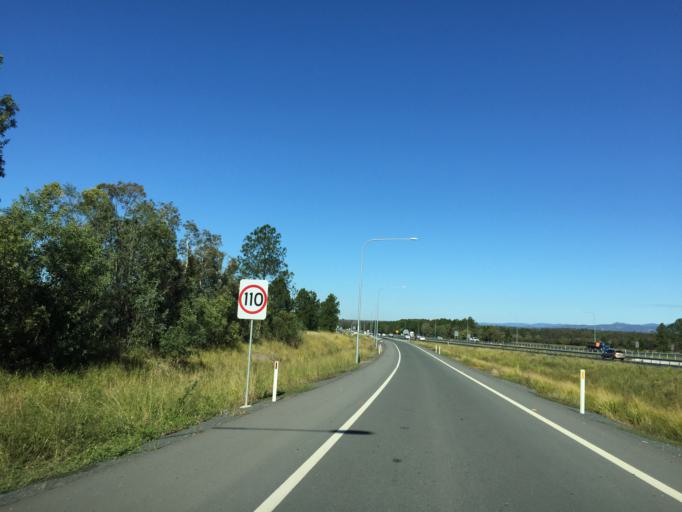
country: AU
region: Queensland
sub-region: Moreton Bay
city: Caboolture
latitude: -27.0421
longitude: 152.9784
